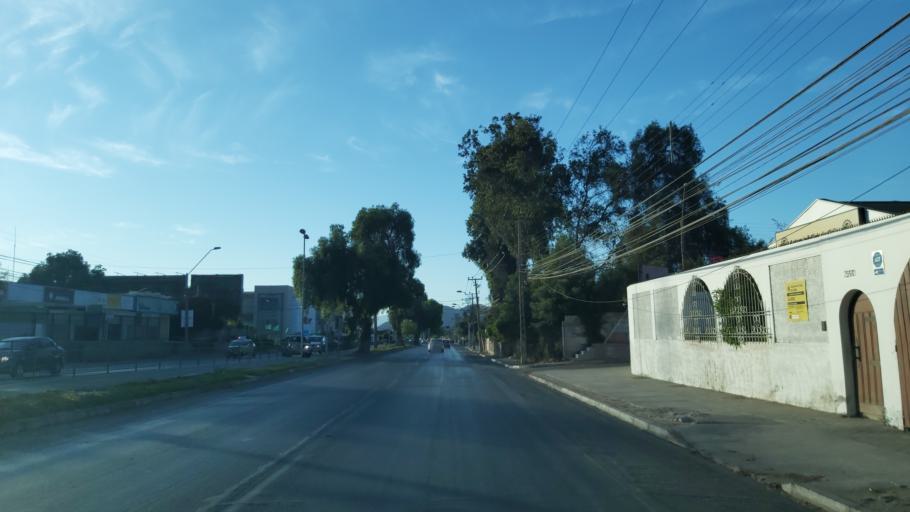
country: CL
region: Atacama
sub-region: Provincia de Copiapo
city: Copiapo
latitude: -27.3831
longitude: -70.3153
